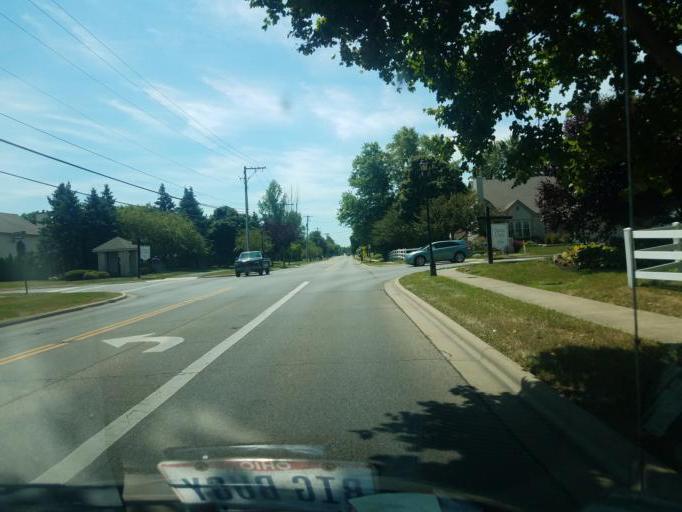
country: US
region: Ohio
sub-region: Franklin County
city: Grove City
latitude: 39.8683
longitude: -83.0862
